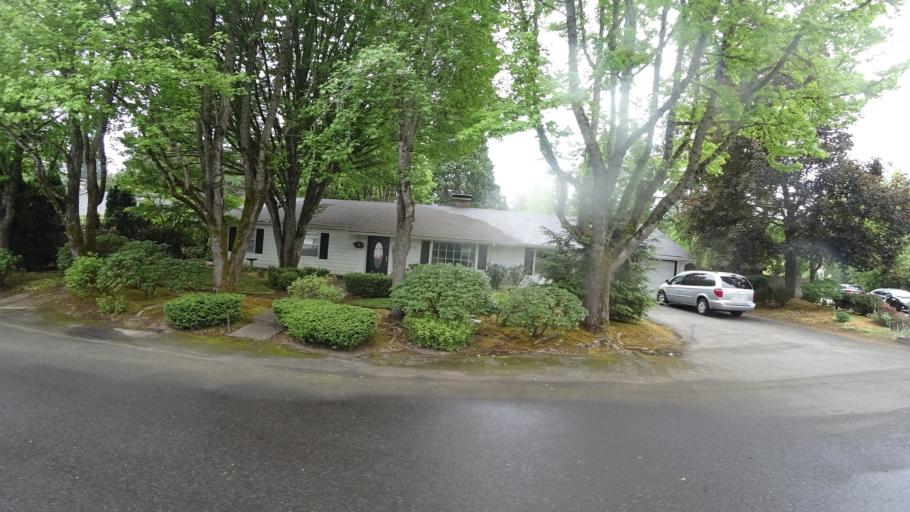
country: US
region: Oregon
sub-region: Washington County
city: Raleigh Hills
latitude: 45.4798
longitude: -122.7674
